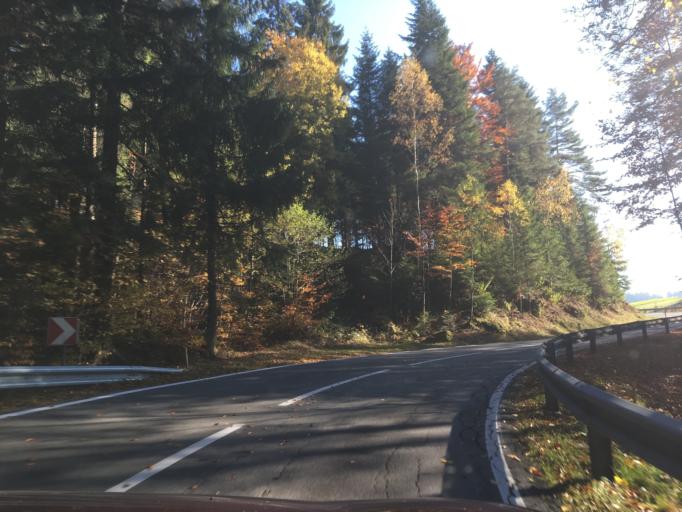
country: AT
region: Lower Austria
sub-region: Politischer Bezirk Zwettl
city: Langschlag
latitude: 48.4614
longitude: 14.7689
